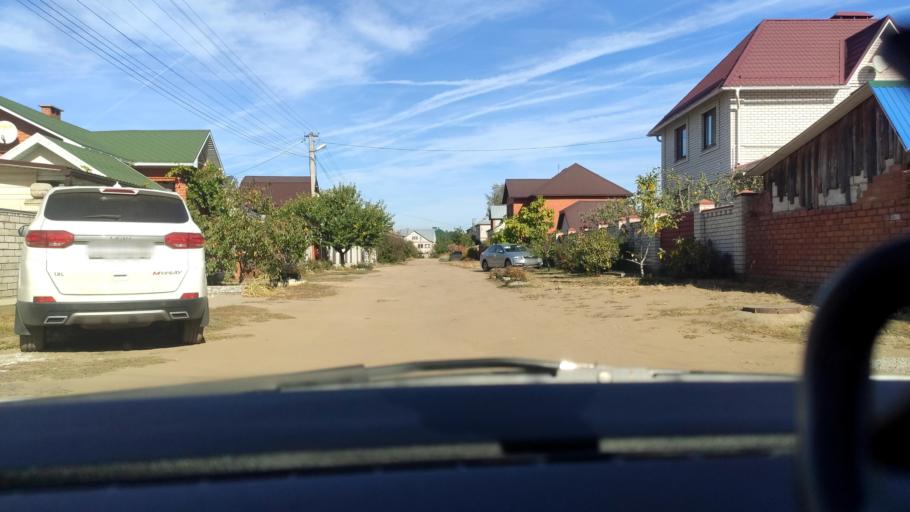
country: RU
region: Voronezj
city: Pridonskoy
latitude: 51.6415
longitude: 39.0841
